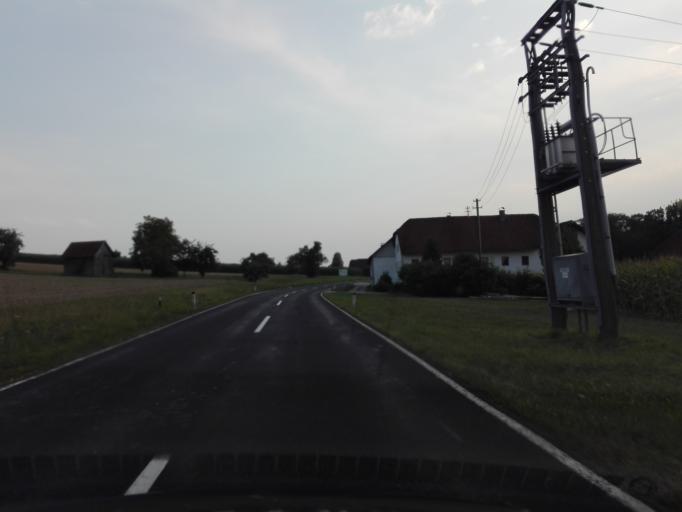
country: AT
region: Upper Austria
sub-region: Politischer Bezirk Grieskirchen
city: Grieskirchen
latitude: 48.2709
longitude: 13.8199
